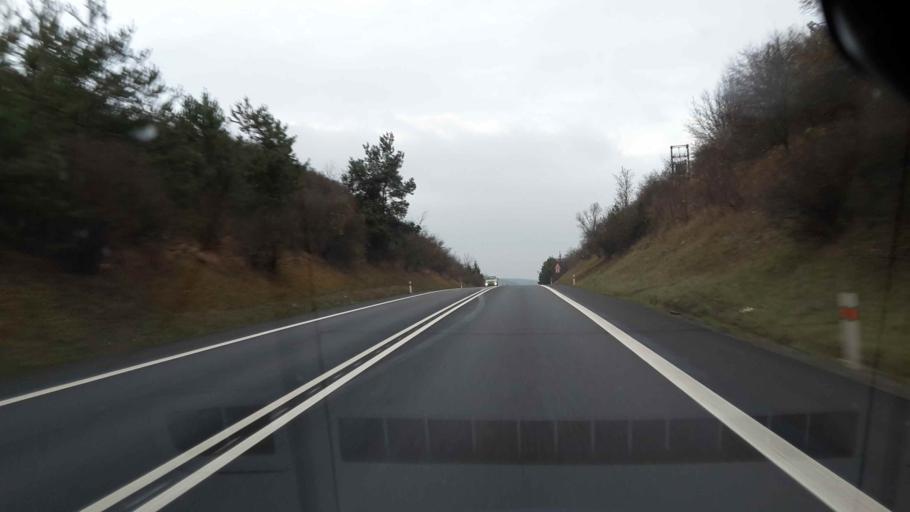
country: CZ
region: South Moravian
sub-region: Okres Brno-Venkov
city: Lelekovice
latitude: 49.2986
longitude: 16.5576
